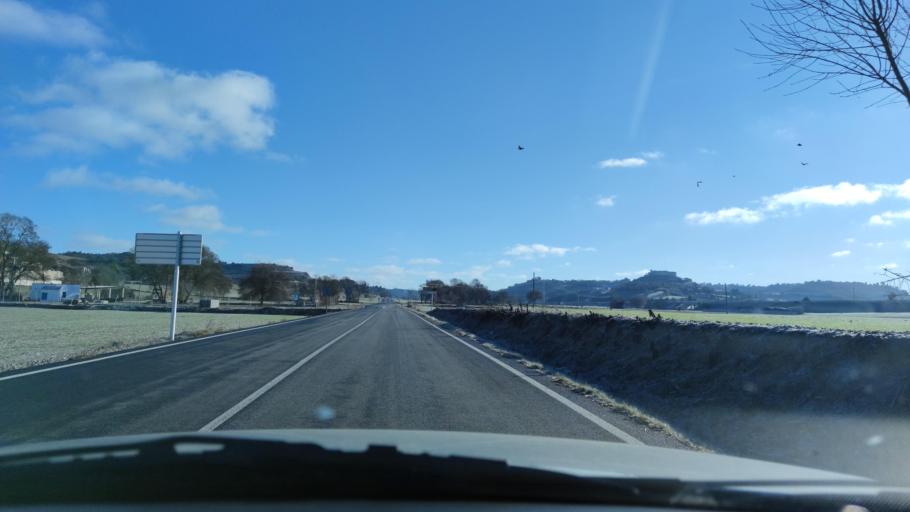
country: ES
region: Catalonia
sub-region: Provincia de Lleida
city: Cervera
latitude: 41.6942
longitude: 1.3216
